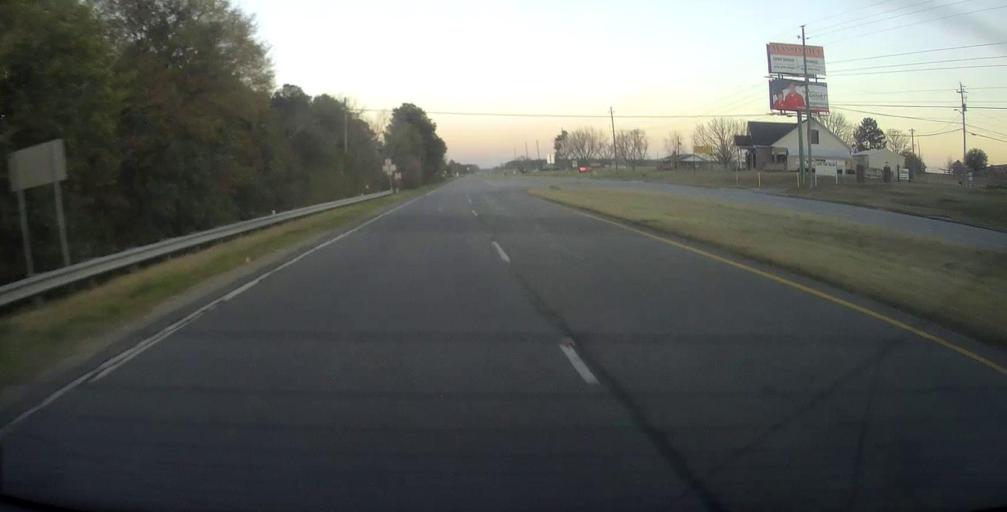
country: US
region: Georgia
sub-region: Dodge County
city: Eastman
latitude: 32.1730
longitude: -83.1591
